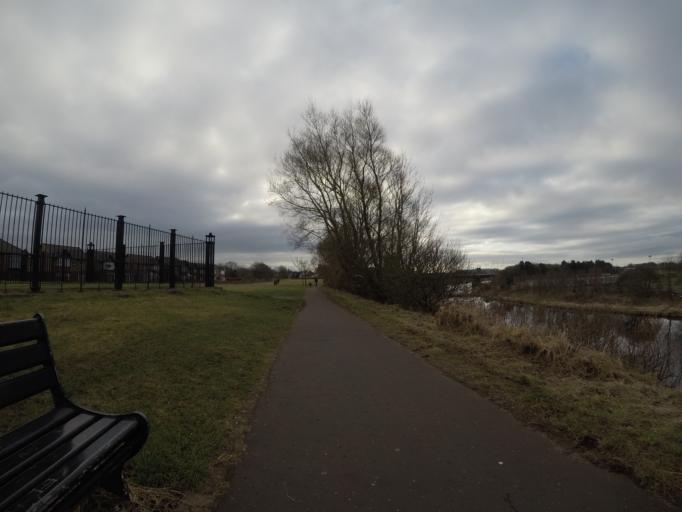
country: GB
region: Scotland
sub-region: North Ayrshire
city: Irvine
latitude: 55.6210
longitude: -4.6743
